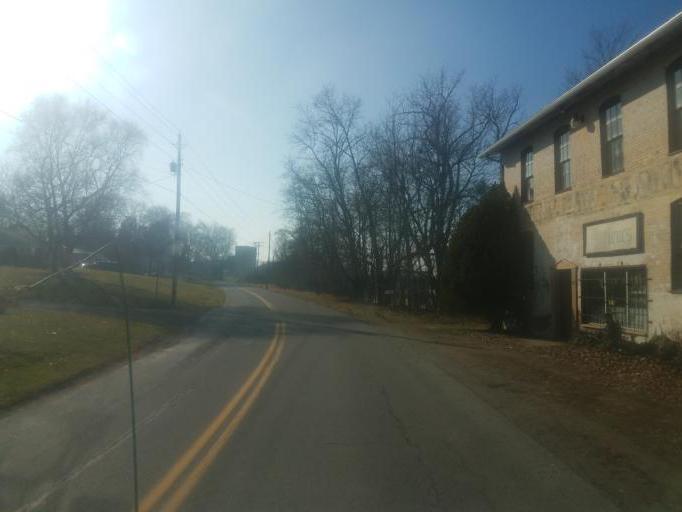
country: US
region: Ohio
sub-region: Seneca County
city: Tiffin
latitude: 41.1223
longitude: -83.1716
